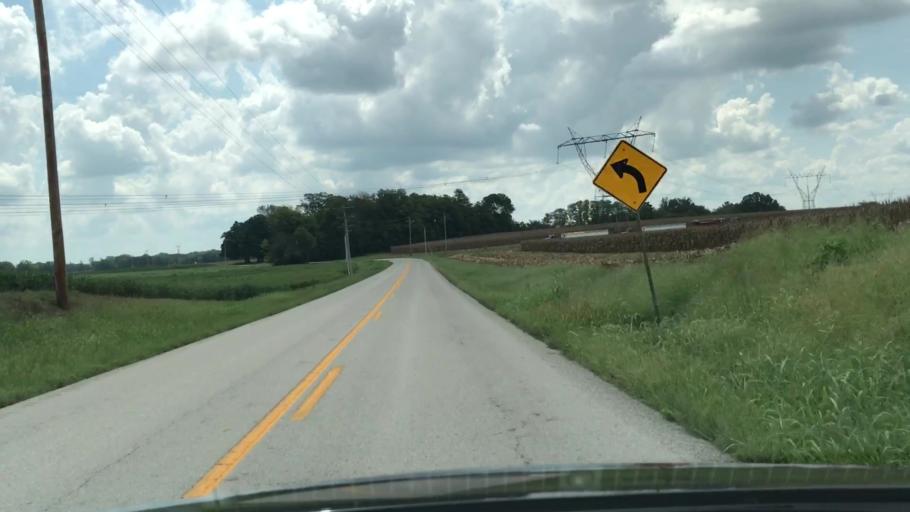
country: US
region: Kentucky
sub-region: Todd County
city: Elkton
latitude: 36.7736
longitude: -87.1179
